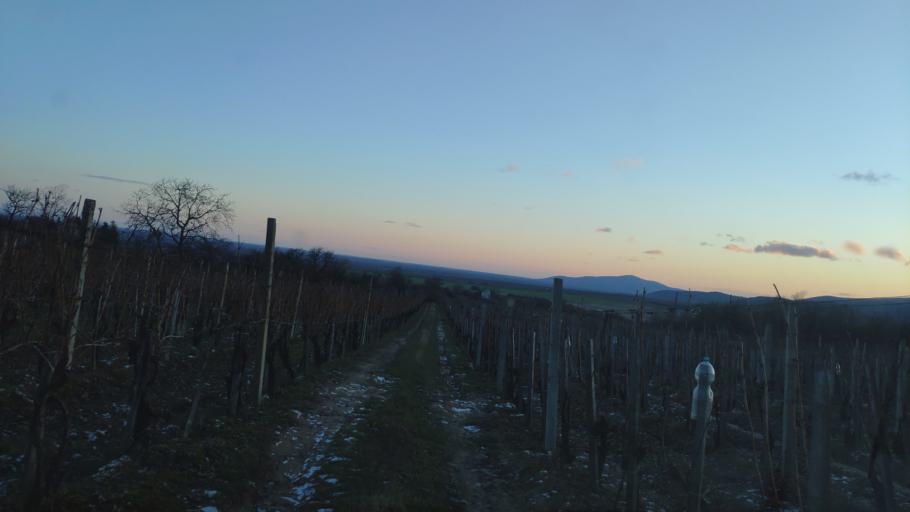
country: HU
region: Borsod-Abauj-Zemplen
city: Olaszliszka
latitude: 48.2755
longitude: 21.3969
